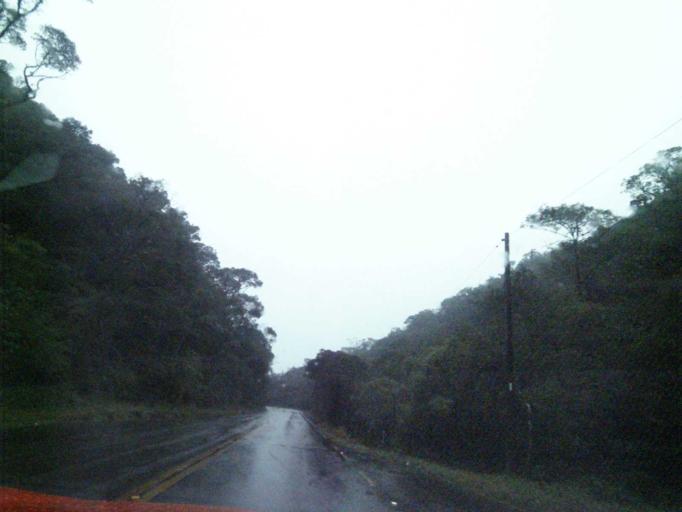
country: BR
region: Santa Catarina
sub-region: Anitapolis
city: Anitapolis
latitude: -27.7657
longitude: -49.0394
